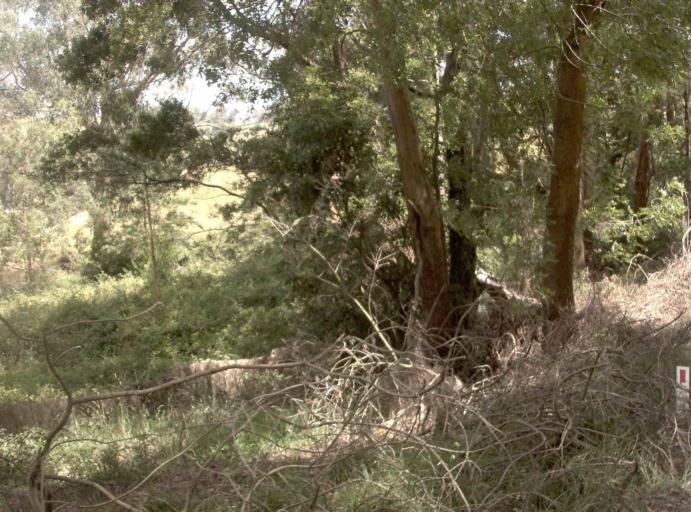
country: AU
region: Victoria
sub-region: Baw Baw
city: Warragul
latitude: -38.2691
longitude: 145.8928
